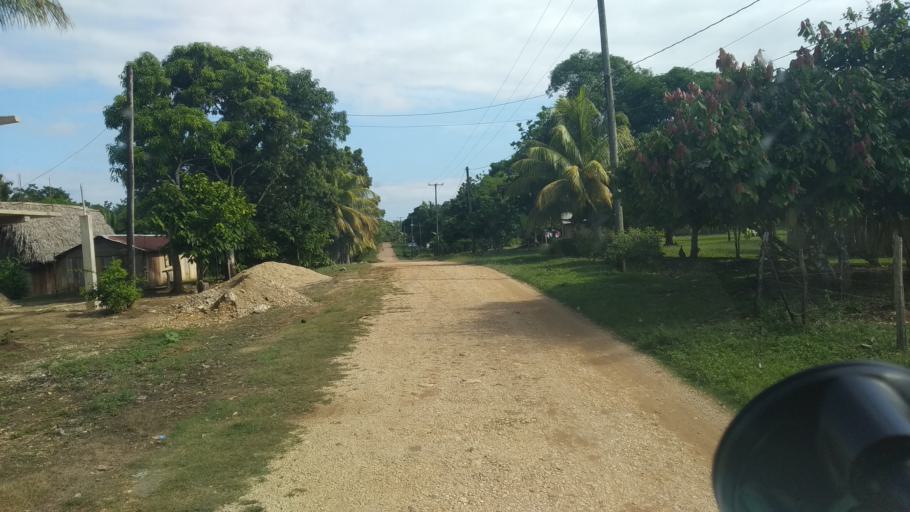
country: BZ
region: Toledo
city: Punta Gorda
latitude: 16.2112
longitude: -88.9118
